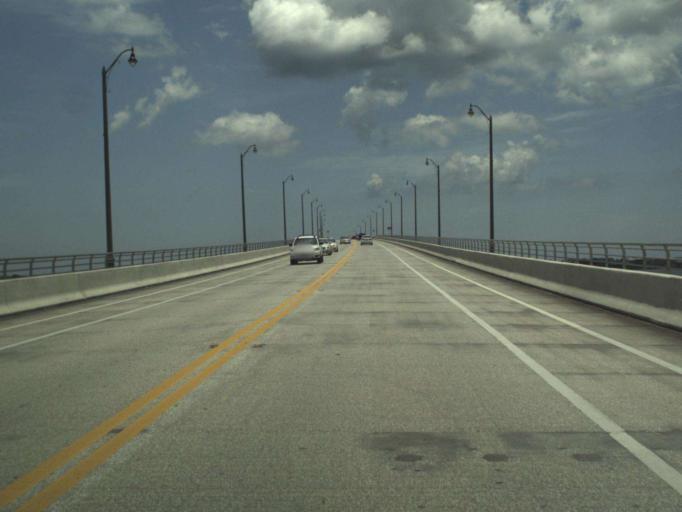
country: US
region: Florida
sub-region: Martin County
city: Sewall's Point
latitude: 27.2050
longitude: -80.1958
